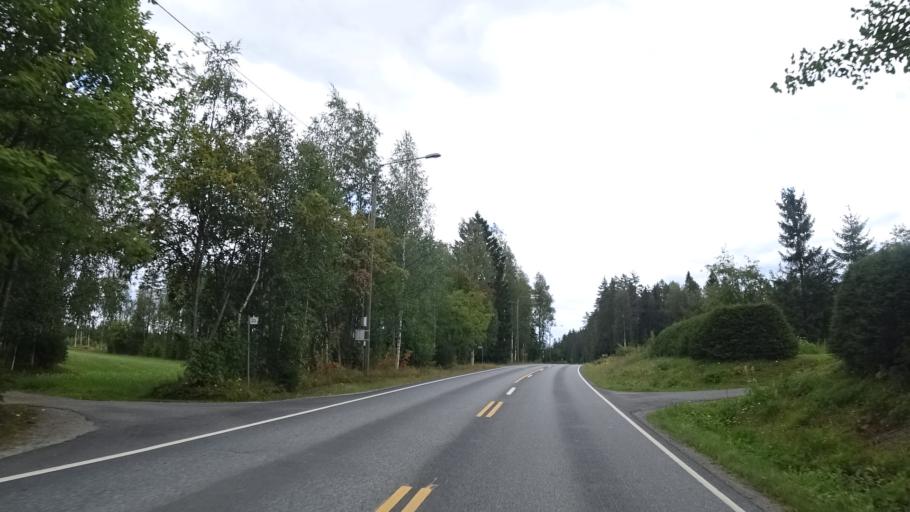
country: FI
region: North Karelia
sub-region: Joensuu
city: Ilomantsi
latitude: 62.6523
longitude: 30.9692
